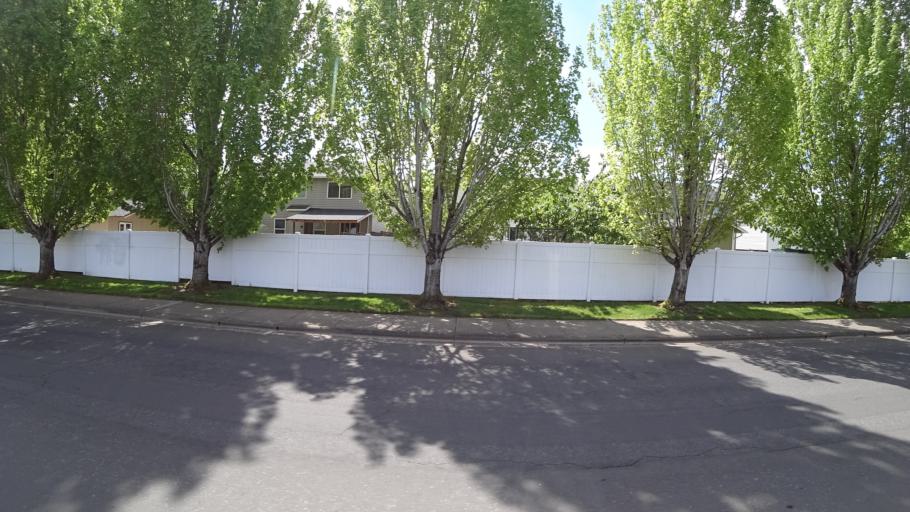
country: US
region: Oregon
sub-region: Washington County
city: Aloha
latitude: 45.5079
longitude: -122.8883
